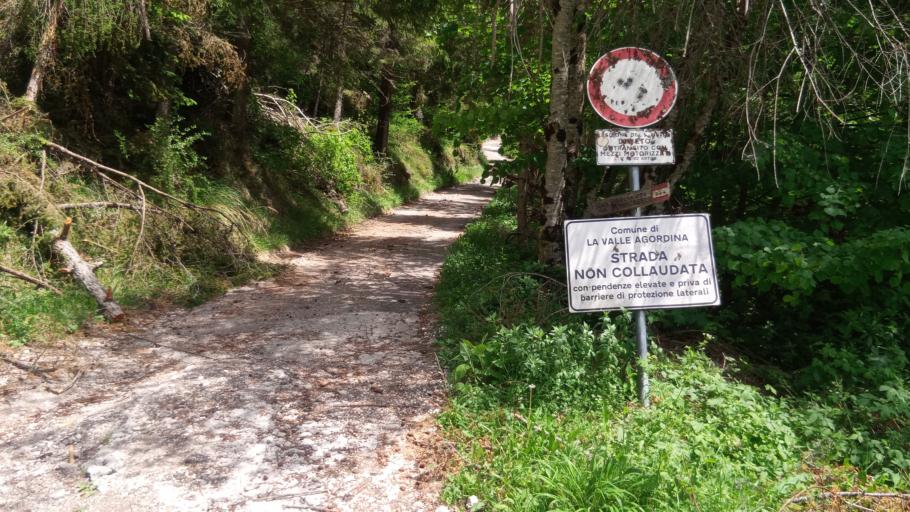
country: IT
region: Veneto
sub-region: Provincia di Belluno
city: La Valle Agordina
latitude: 46.2964
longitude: 12.0938
